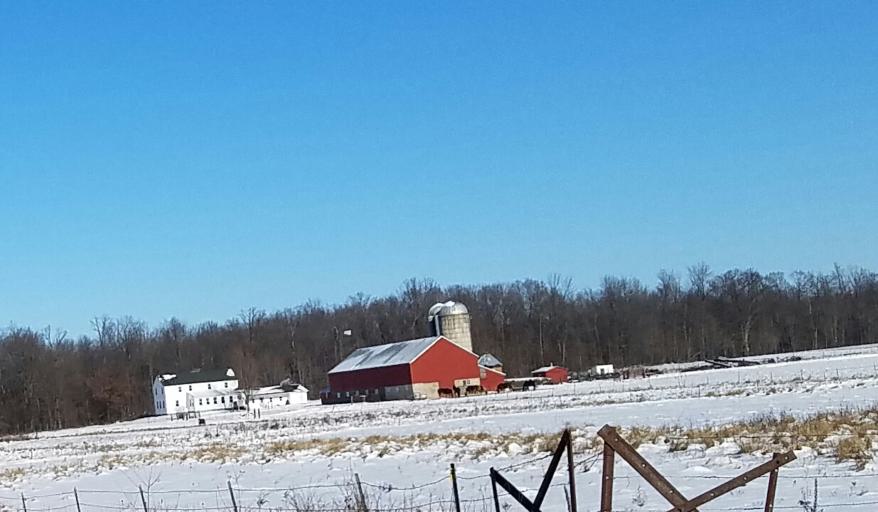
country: US
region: Wisconsin
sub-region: Marathon County
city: Spencer
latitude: 44.5681
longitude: -90.3765
